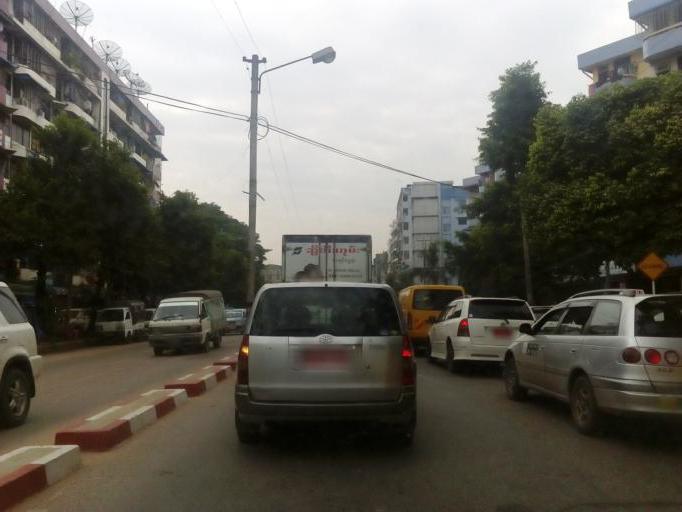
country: MM
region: Yangon
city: Yangon
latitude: 16.8431
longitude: 96.1263
